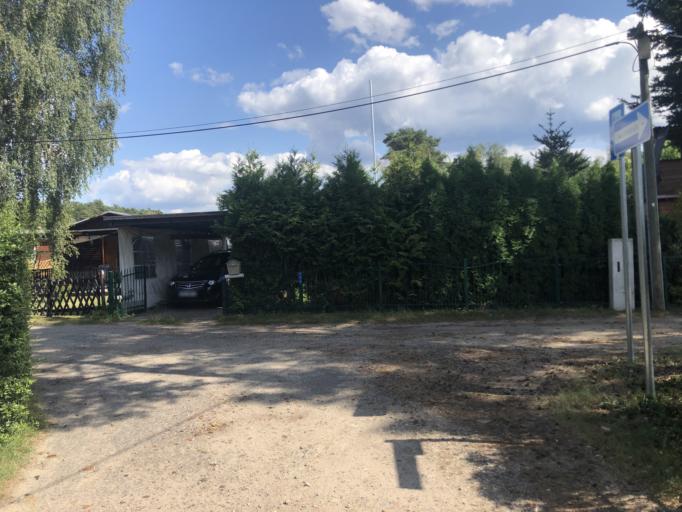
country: DE
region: Brandenburg
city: Mullrose
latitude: 52.2341
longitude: 14.4103
